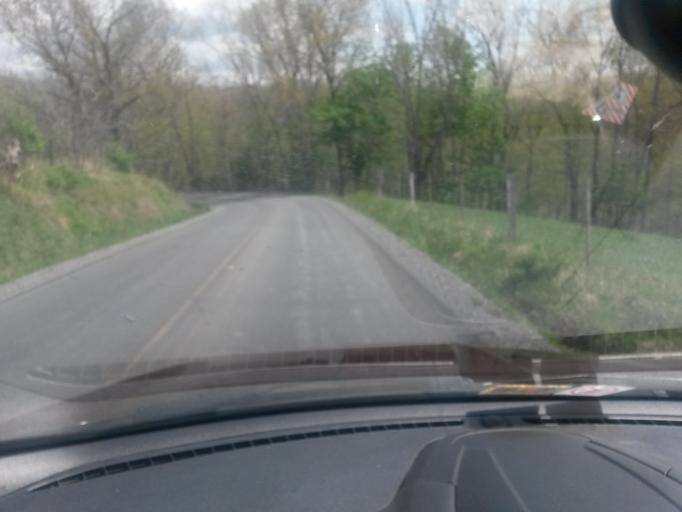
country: US
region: West Virginia
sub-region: Pocahontas County
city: Marlinton
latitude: 38.1072
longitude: -80.2237
